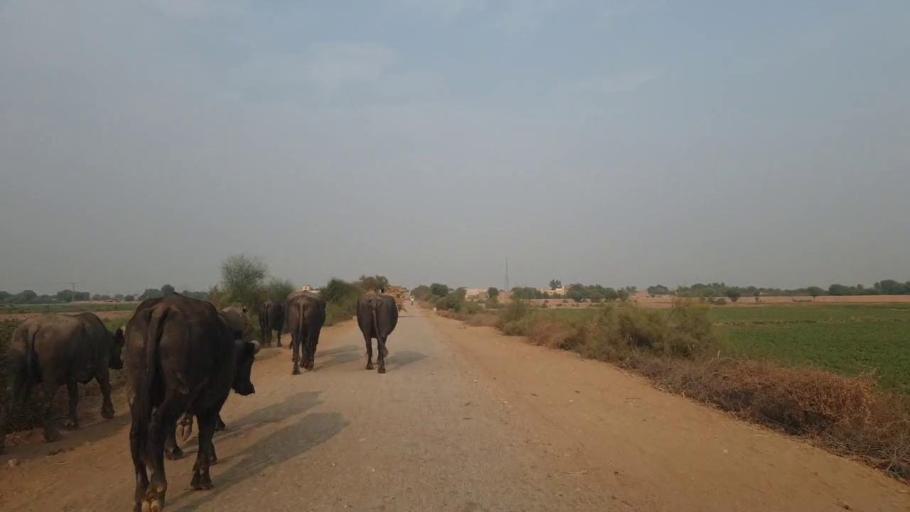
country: PK
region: Sindh
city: Sann
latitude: 26.1343
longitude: 68.0486
